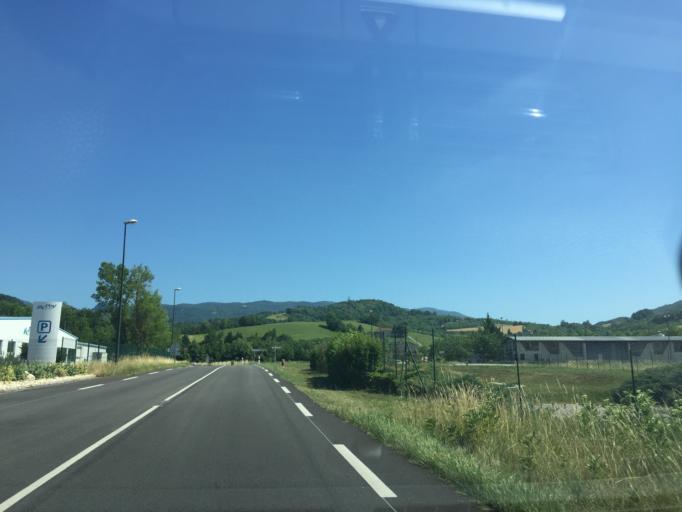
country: FR
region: Rhone-Alpes
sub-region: Departement de l'Isere
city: Saint-Just-de-Claix
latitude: 45.0532
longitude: 5.2657
